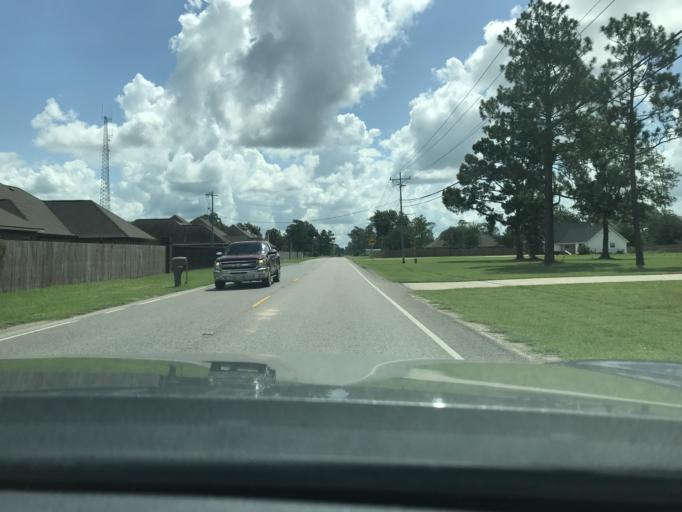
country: US
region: Louisiana
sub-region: Calcasieu Parish
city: Moss Bluff
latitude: 30.3447
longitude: -93.2272
